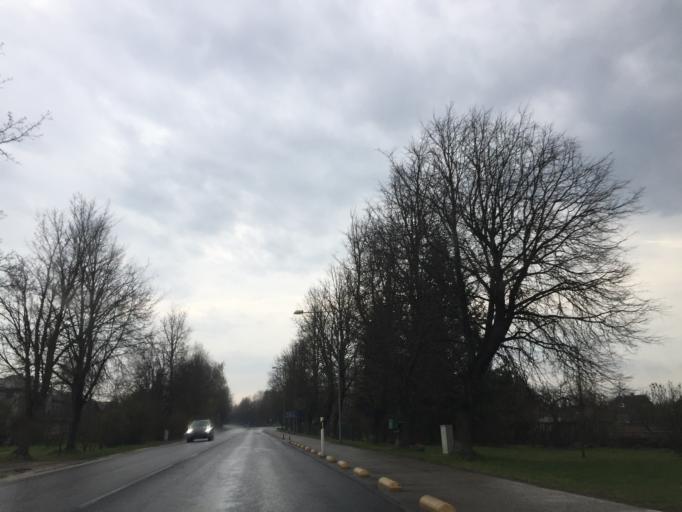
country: EE
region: Tartu
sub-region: UElenurme vald
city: Ulenurme
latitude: 58.3301
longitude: 26.7186
